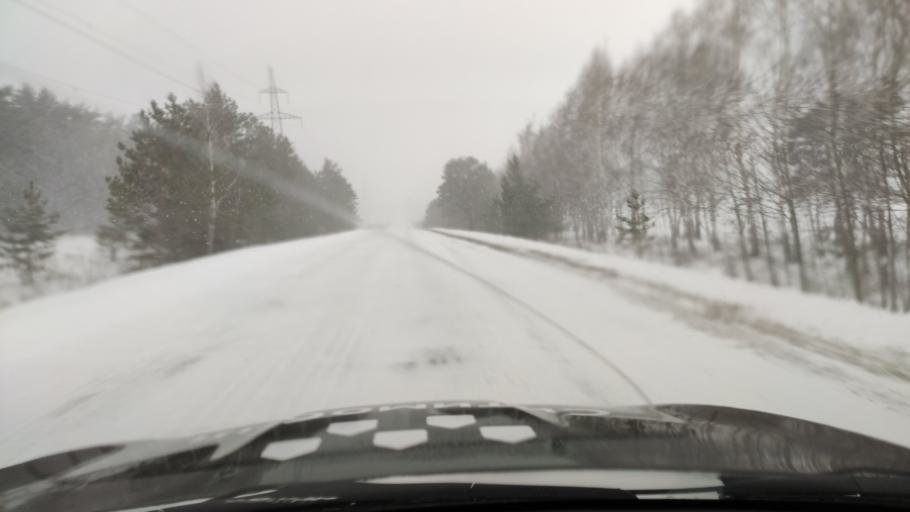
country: RU
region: Samara
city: Povolzhskiy
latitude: 53.5237
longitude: 49.7033
